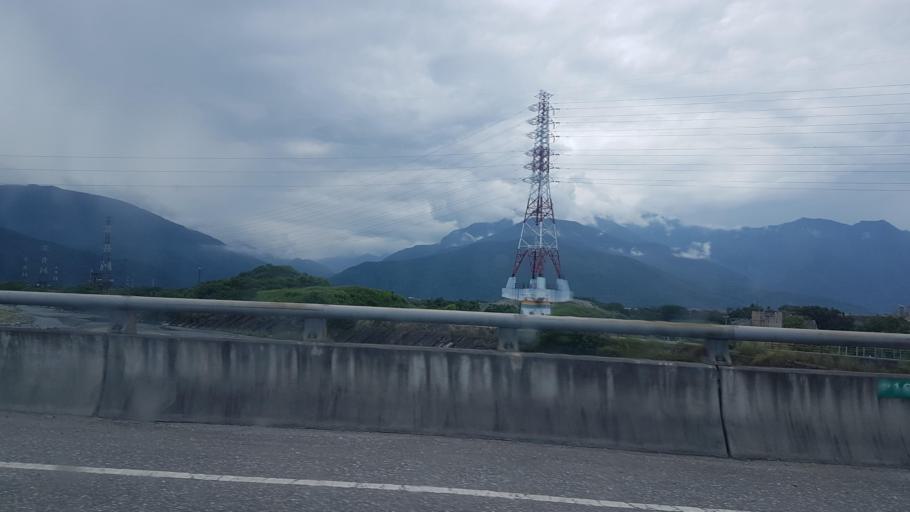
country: TW
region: Taiwan
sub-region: Hualien
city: Hualian
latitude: 23.9195
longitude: 121.5847
